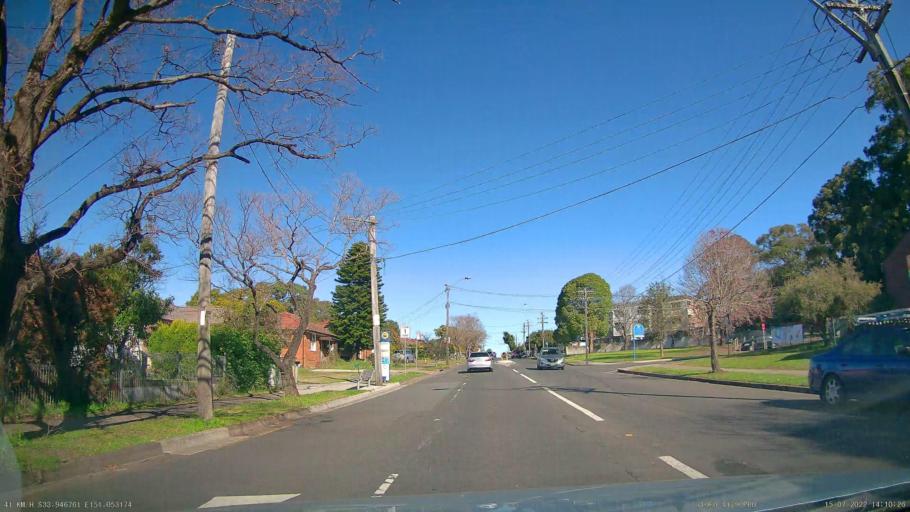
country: AU
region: New South Wales
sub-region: Hurstville
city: Peakhurst
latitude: -33.9469
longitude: 151.0531
